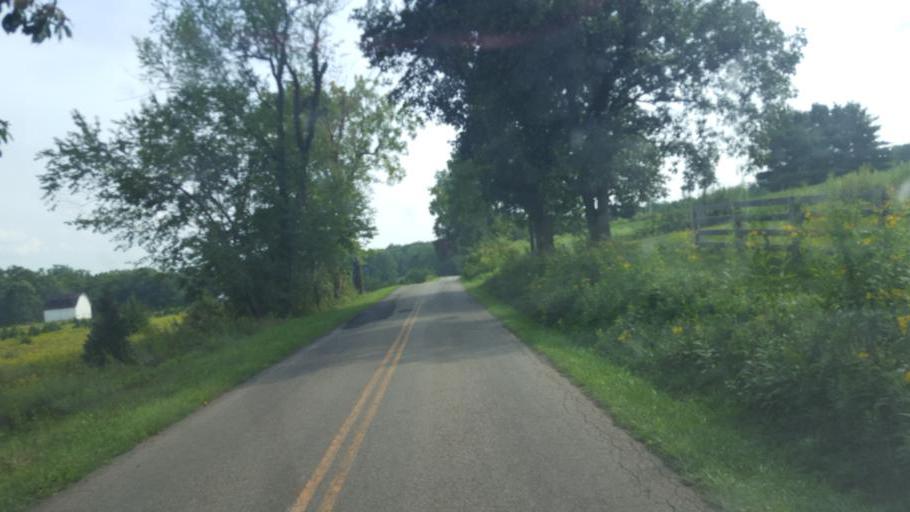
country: US
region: Ohio
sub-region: Knox County
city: Gambier
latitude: 40.3511
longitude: -82.3861
